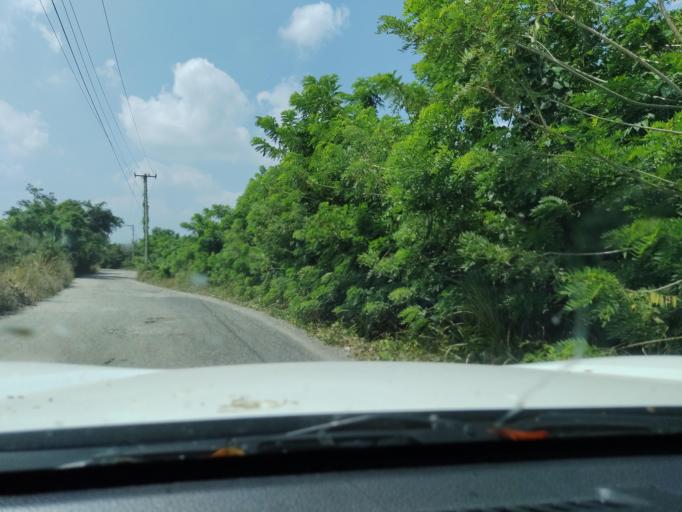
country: MX
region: Veracruz
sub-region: Atzalan
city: Colonias Pedernales
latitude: 20.0619
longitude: -97.0274
